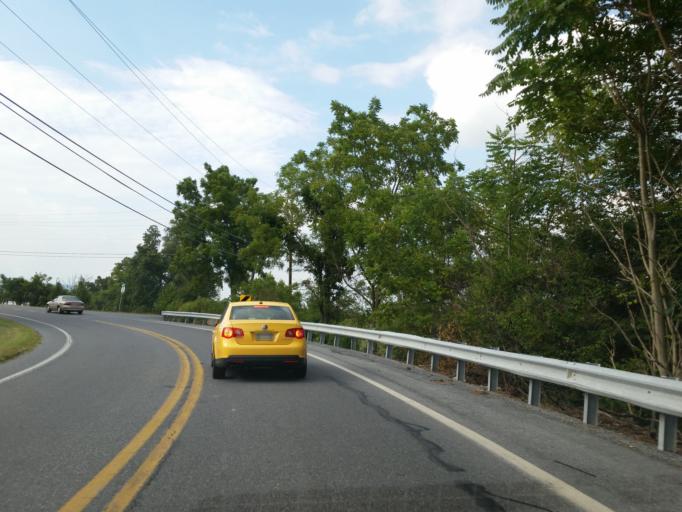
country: US
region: Pennsylvania
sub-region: Lebanon County
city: Jonestown
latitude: 40.3976
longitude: -76.5220
